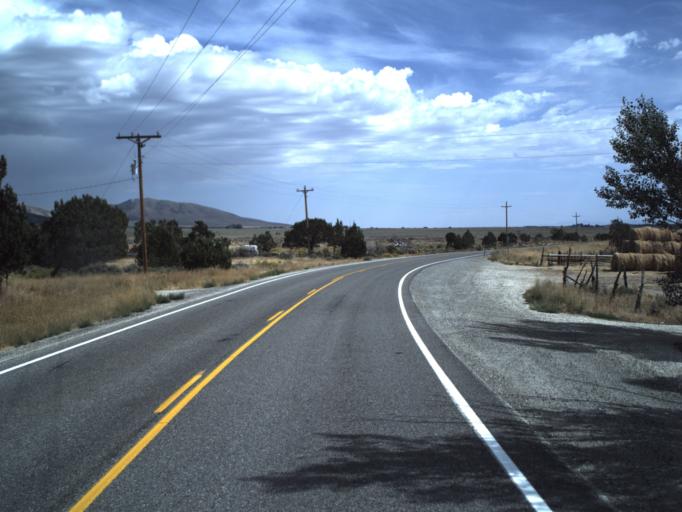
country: US
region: Idaho
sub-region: Cassia County
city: Burley
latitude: 41.8195
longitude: -113.4067
